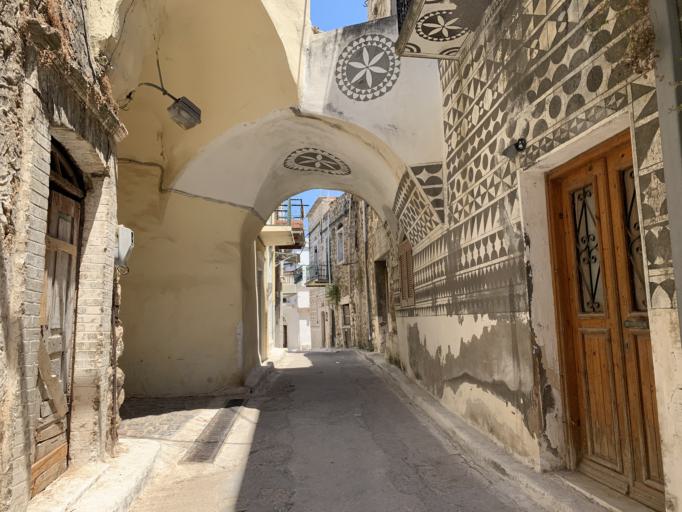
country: GR
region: North Aegean
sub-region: Chios
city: Thymiana
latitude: 38.2281
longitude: 25.9997
